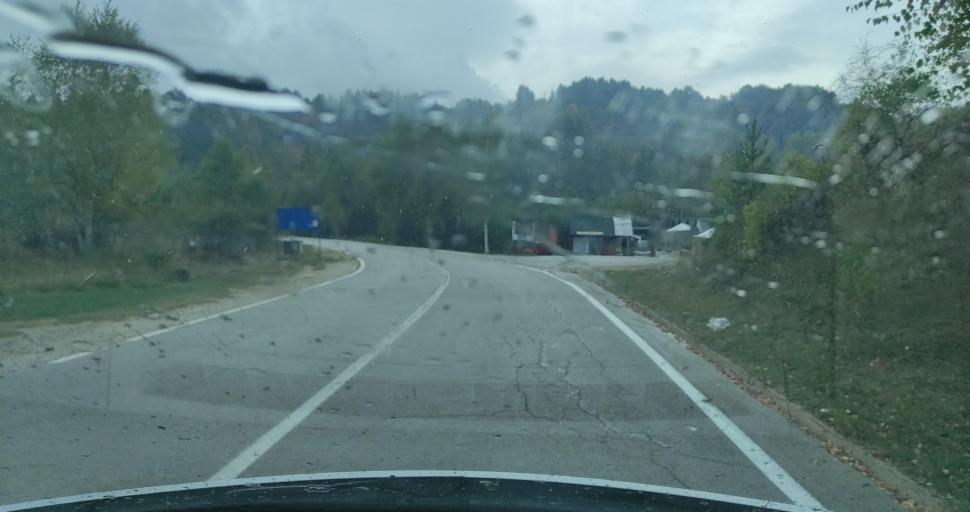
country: RS
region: Central Serbia
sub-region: Jablanicki Okrug
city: Crna Trava
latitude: 42.7339
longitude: 22.3312
